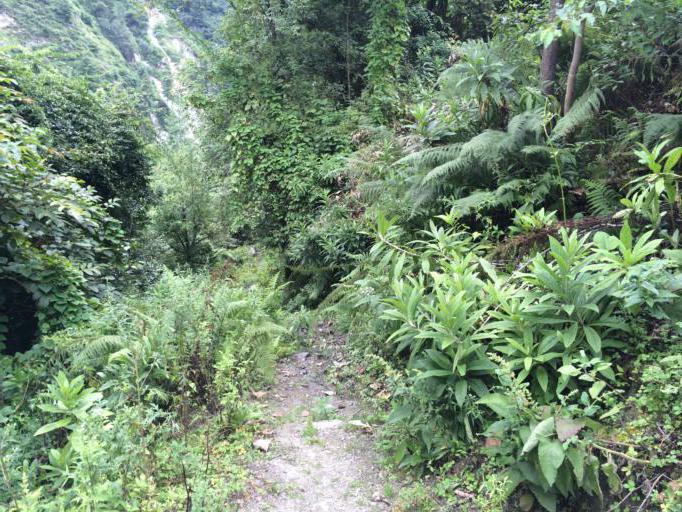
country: NP
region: Western Region
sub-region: Gandaki Zone
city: Chame
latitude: 28.5337
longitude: 84.3269
